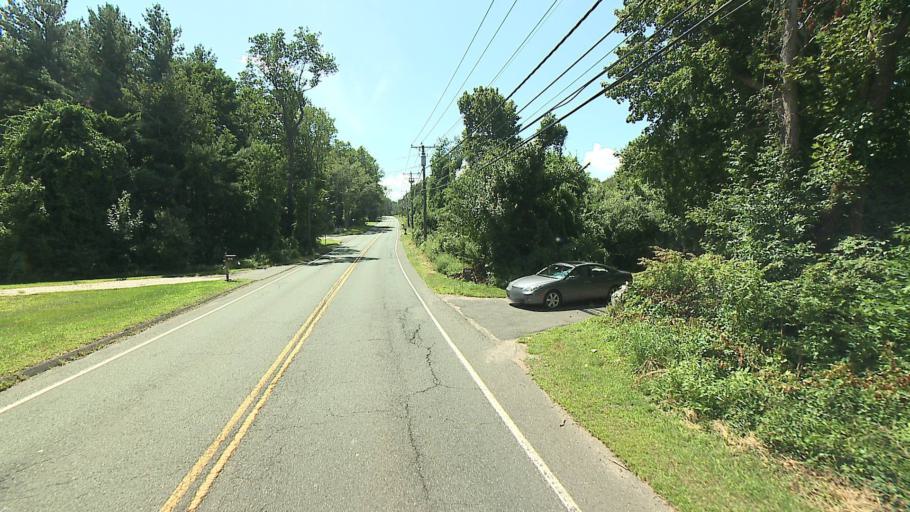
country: US
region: Connecticut
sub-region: Fairfield County
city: Trumbull
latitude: 41.3482
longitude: -73.1984
